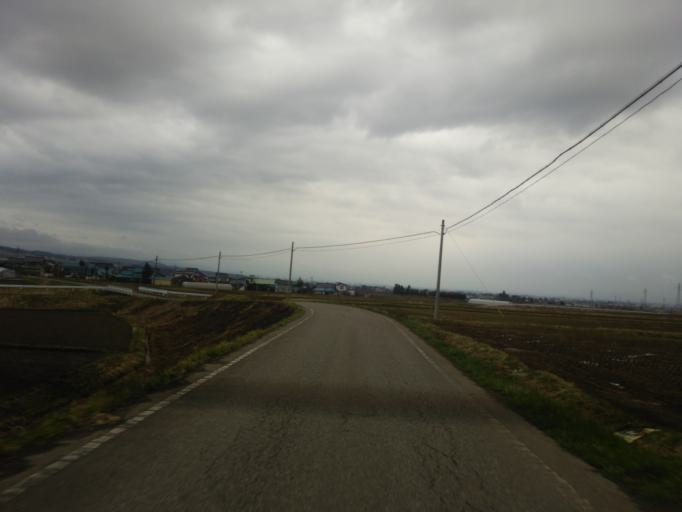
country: JP
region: Fukushima
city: Kitakata
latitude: 37.6541
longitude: 139.9168
